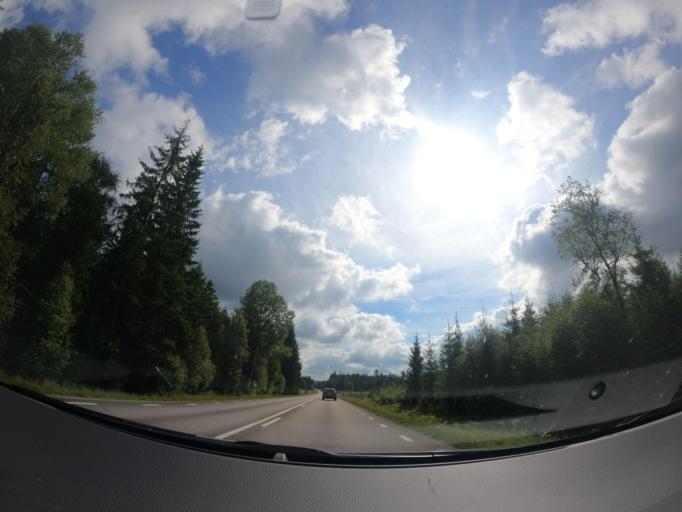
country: SE
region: Halland
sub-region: Hylte Kommun
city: Hyltebruk
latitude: 57.1292
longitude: 13.2303
